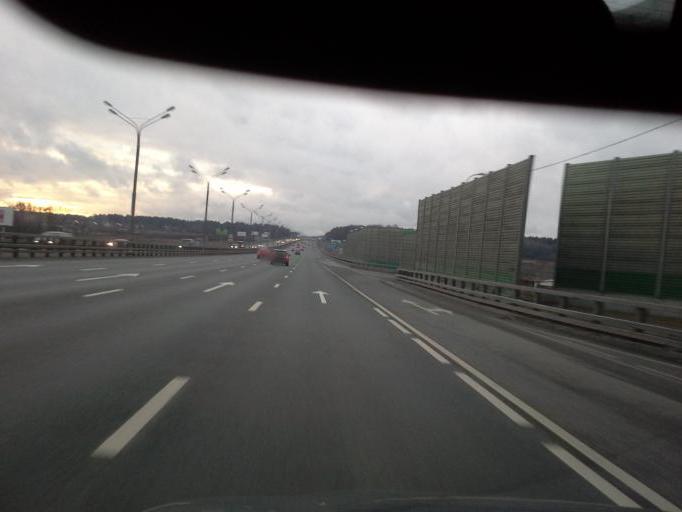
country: RU
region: Moskovskaya
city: Kokoshkino
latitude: 55.6217
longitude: 37.1351
